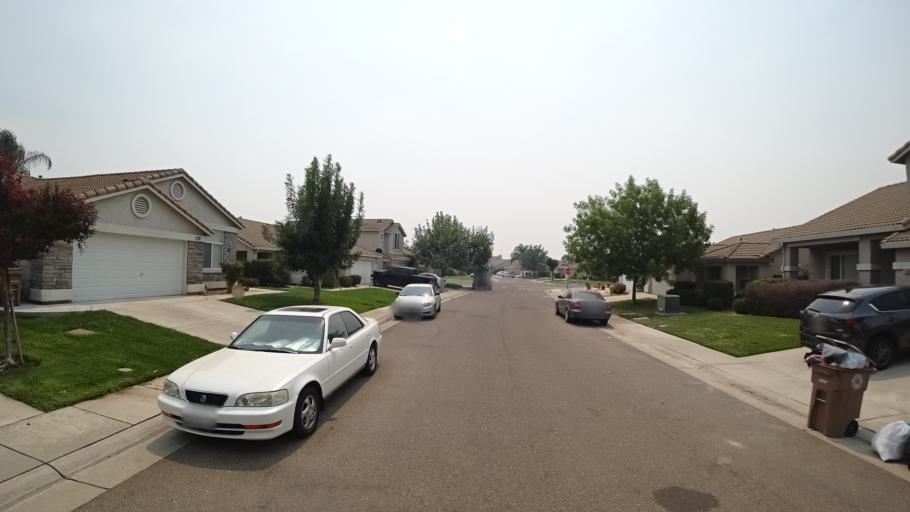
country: US
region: California
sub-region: Sacramento County
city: Laguna
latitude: 38.3998
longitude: -121.4329
